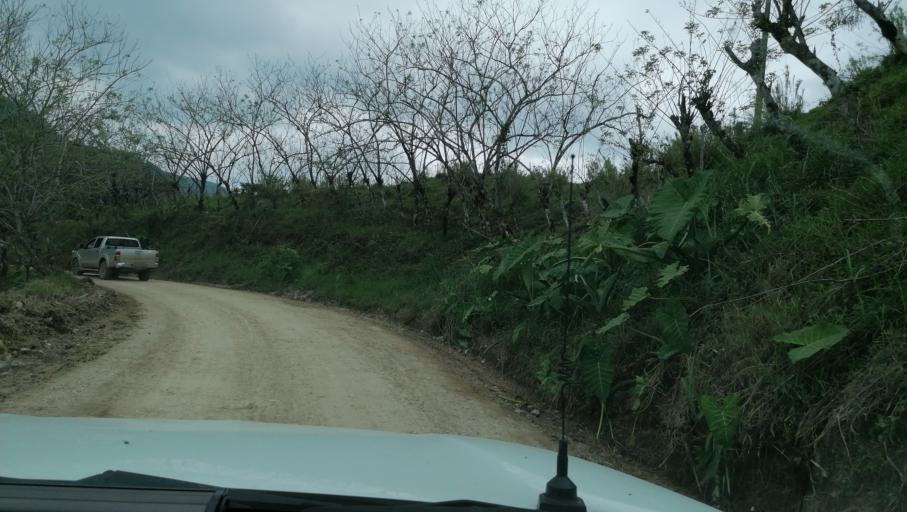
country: MX
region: Chiapas
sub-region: Ocotepec
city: San Pablo Huacano
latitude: 17.2694
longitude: -93.2580
